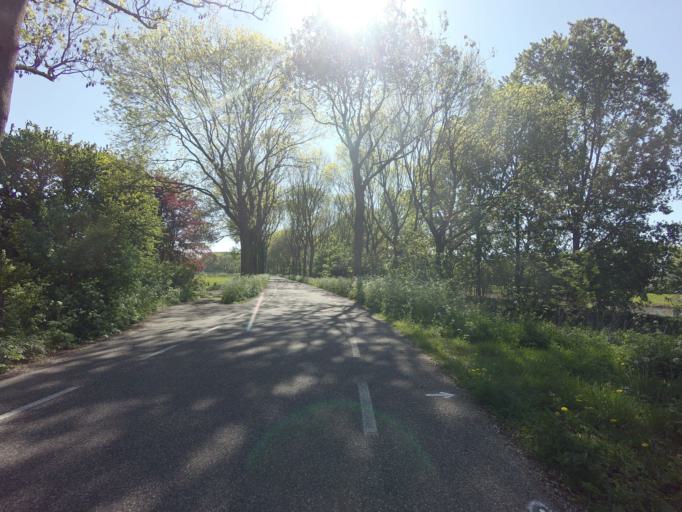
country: NL
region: North Brabant
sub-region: Gemeente Moerdijk
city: Klundert
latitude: 51.6679
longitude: 4.6114
